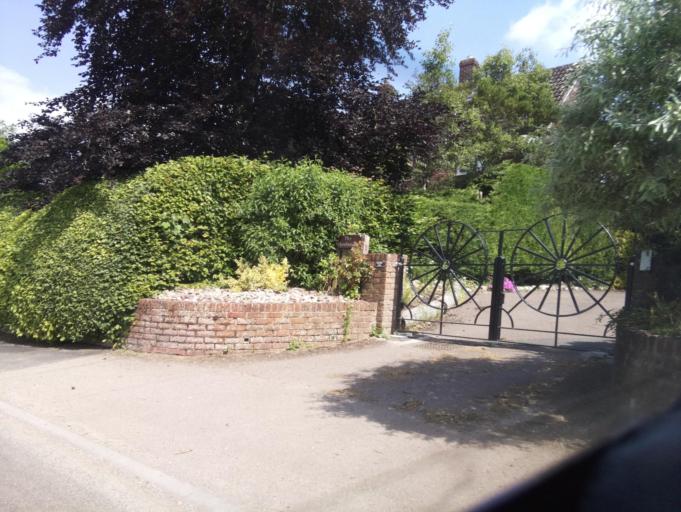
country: GB
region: England
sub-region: Wiltshire
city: Rushall
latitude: 51.3045
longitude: -1.8211
